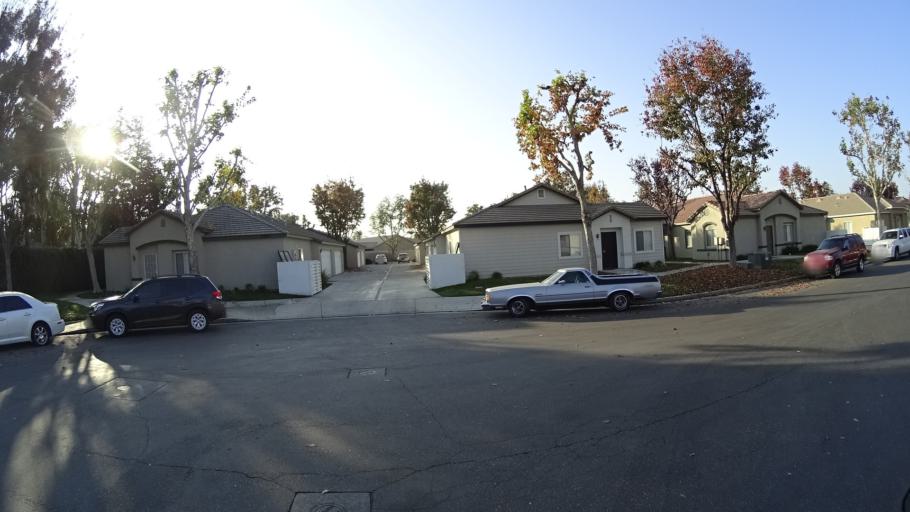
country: US
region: California
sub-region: Kern County
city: Rosedale
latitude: 35.3796
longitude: -119.1464
